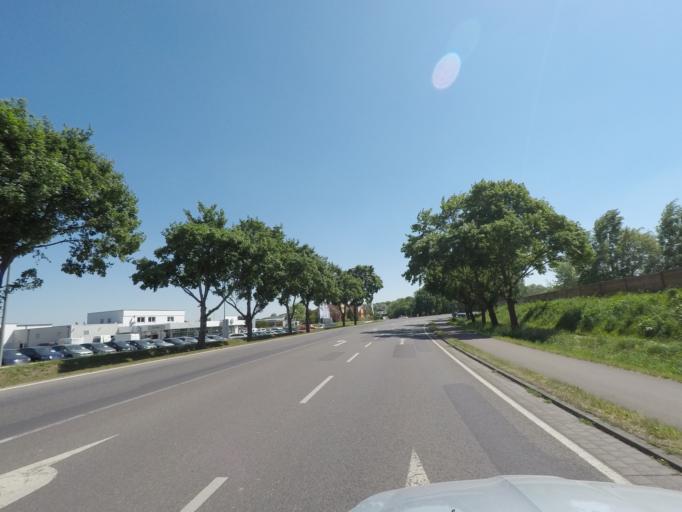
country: DE
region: Brandenburg
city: Melchow
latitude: 52.8488
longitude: 13.6884
